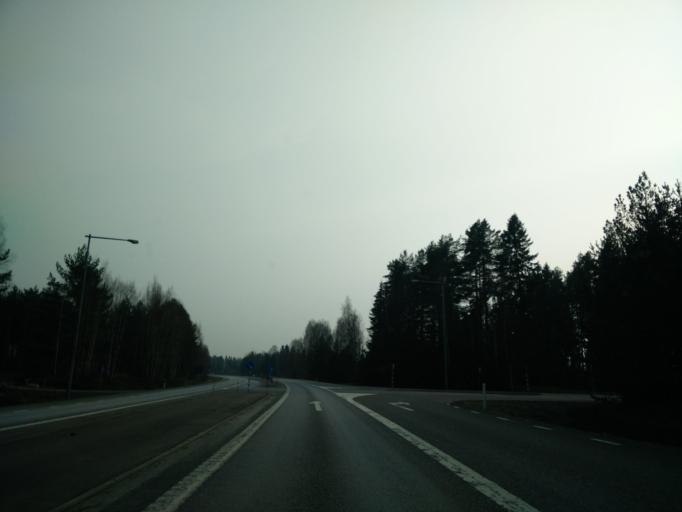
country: SE
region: Vaermland
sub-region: Forshaga Kommun
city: Forshaga
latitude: 59.4829
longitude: 13.4127
